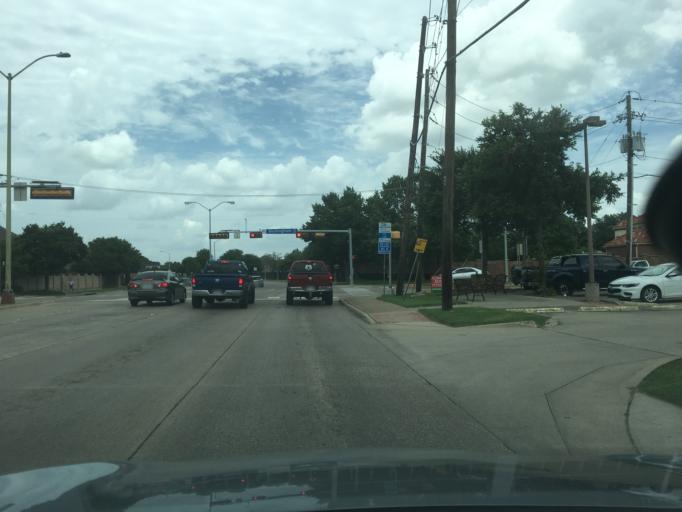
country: US
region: Texas
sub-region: Dallas County
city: Richardson
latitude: 32.9309
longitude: -96.7180
